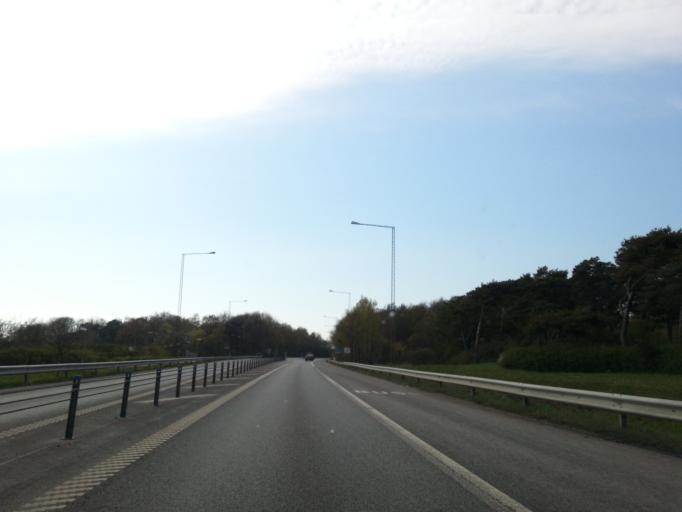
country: SE
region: Skane
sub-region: Trelleborgs Kommun
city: Skare
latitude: 55.3770
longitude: 13.0989
